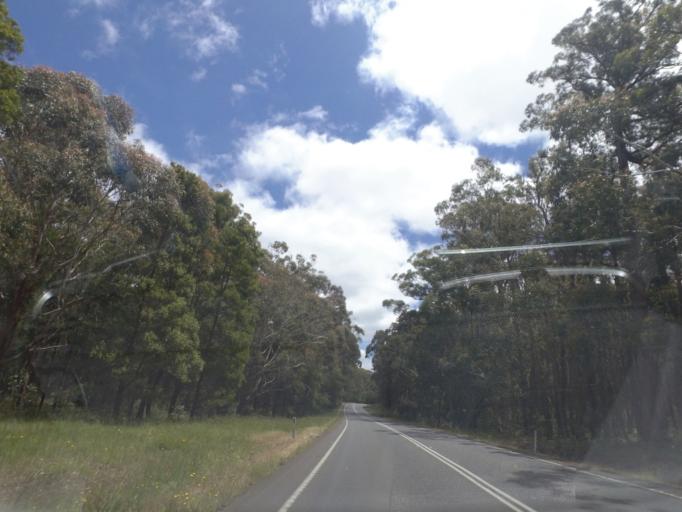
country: AU
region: Victoria
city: Brown Hill
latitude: -37.5051
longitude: 144.1595
